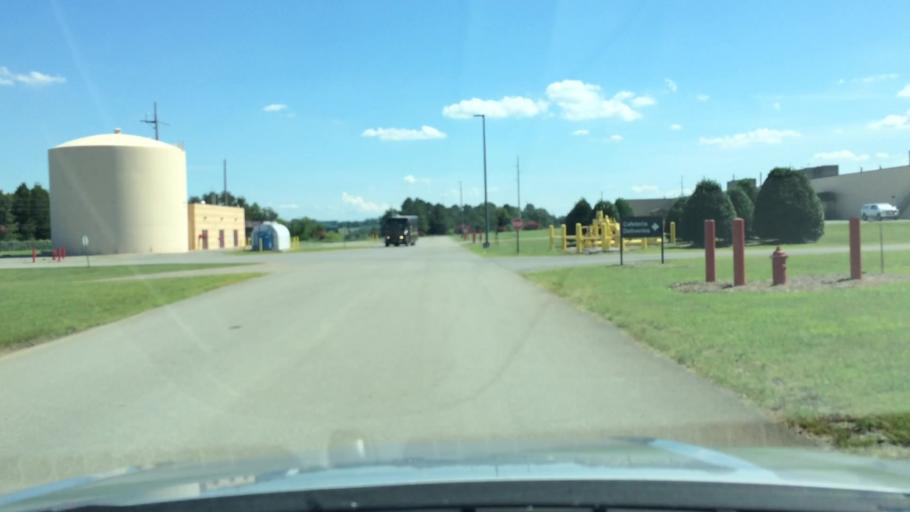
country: US
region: Tennessee
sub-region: McMinn County
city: Athens
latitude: 35.4758
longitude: -84.6425
